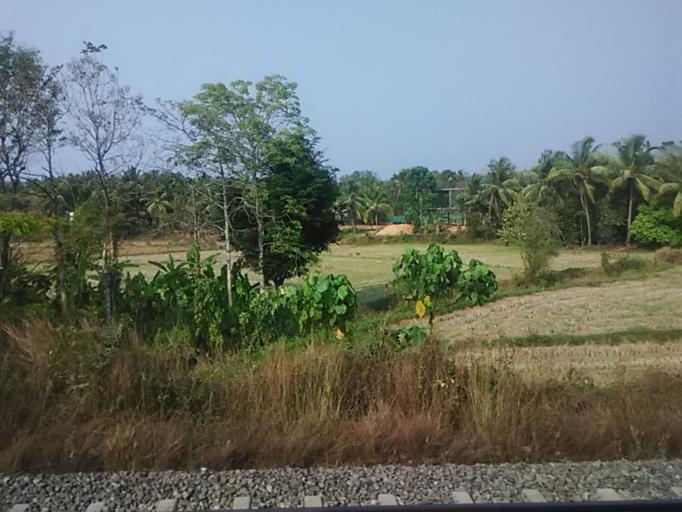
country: IN
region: Kerala
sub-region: Palakkad district
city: Shoranur
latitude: 10.8326
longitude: 76.1250
